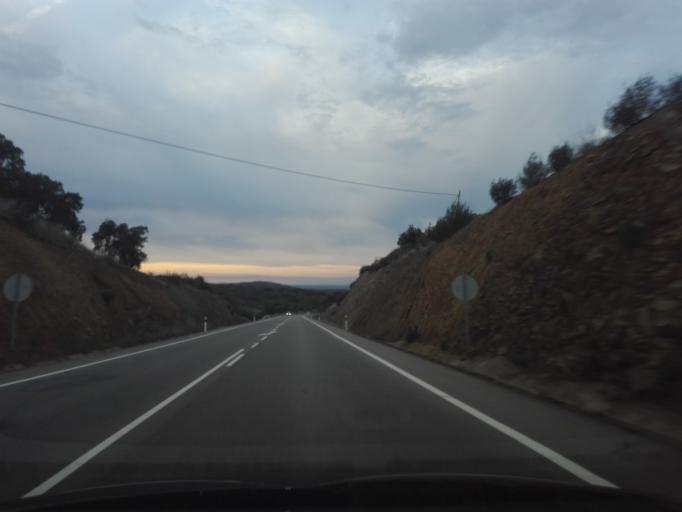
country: ES
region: Extremadura
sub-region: Provincia de Caceres
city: Pedroso de Acim
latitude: 39.8263
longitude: -6.3755
